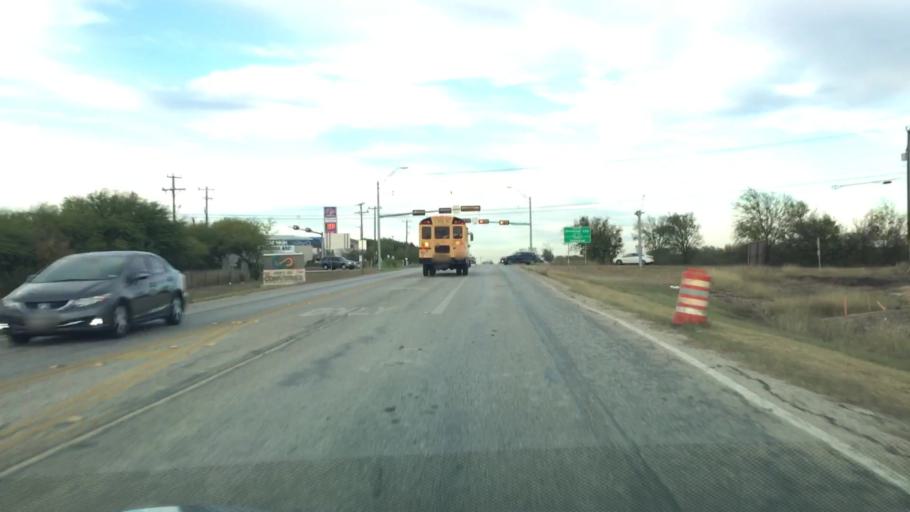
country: US
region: Texas
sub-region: Bexar County
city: Converse
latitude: 29.5265
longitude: -98.3095
